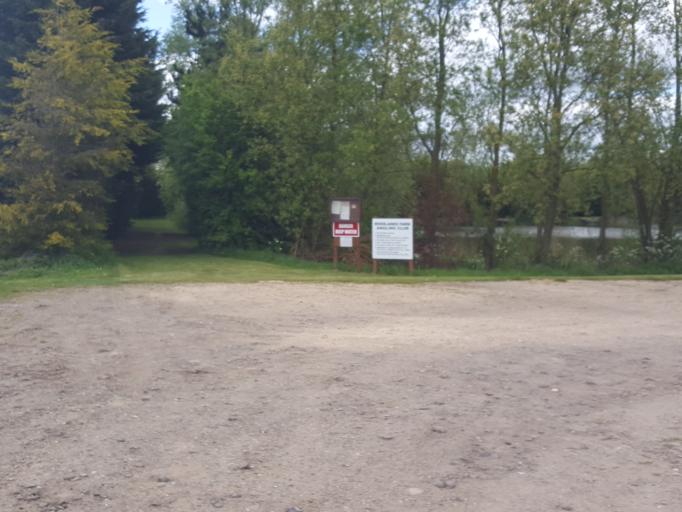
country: GB
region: England
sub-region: Essex
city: Frinton-on-Sea
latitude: 51.8319
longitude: 1.2000
